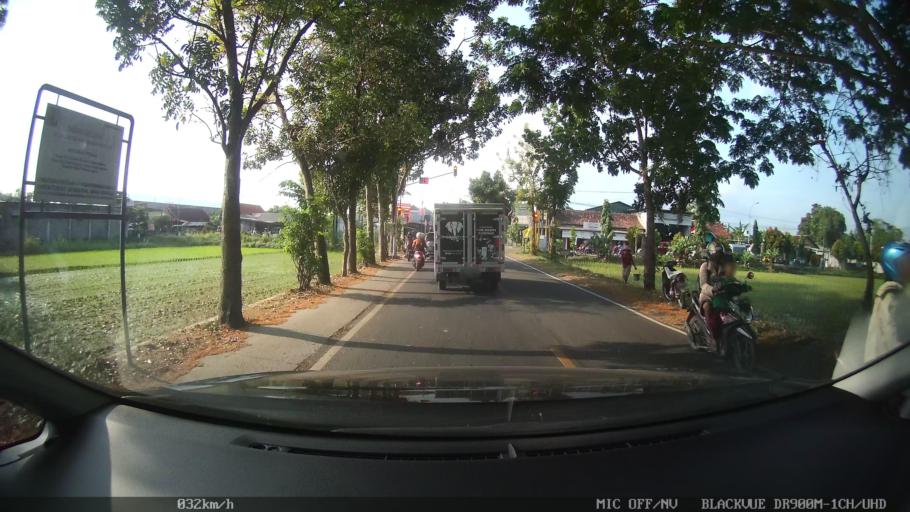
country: ID
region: Daerah Istimewa Yogyakarta
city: Bantul
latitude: -7.8791
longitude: 110.3197
